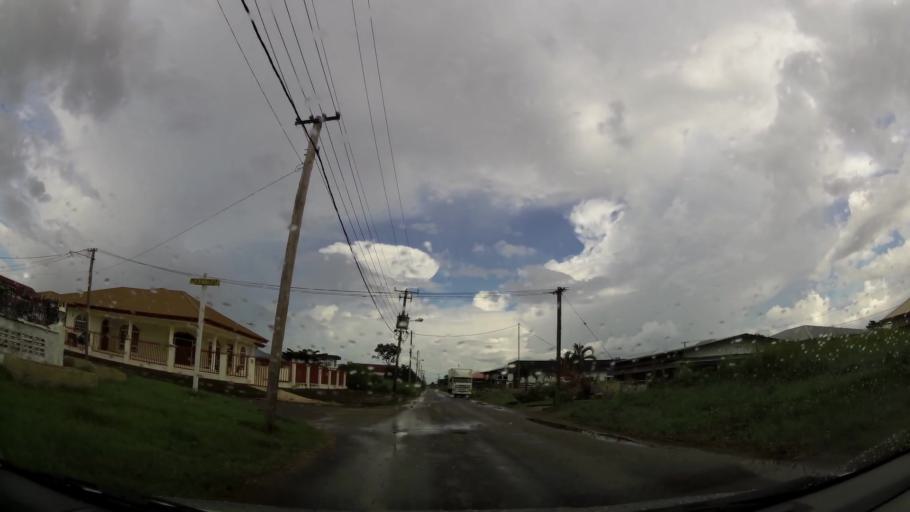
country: SR
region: Commewijne
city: Nieuw Amsterdam
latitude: 5.8578
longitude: -55.1167
